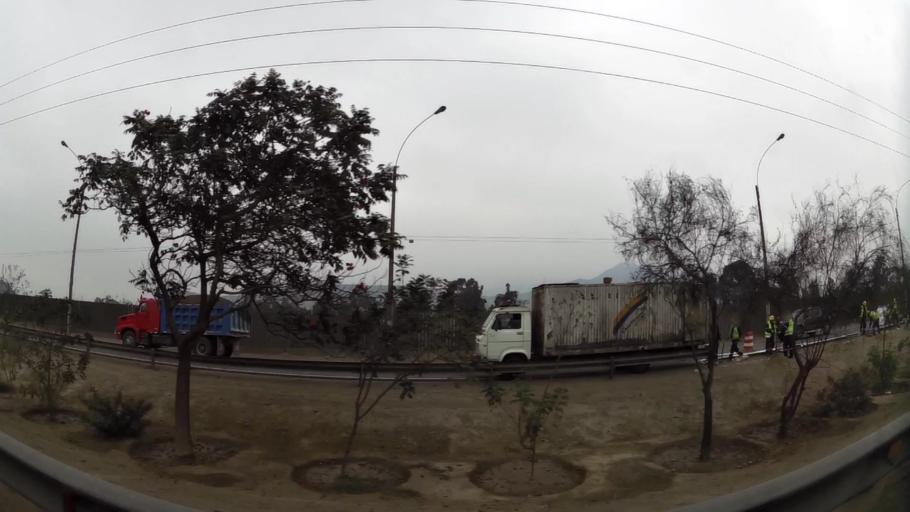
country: PE
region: Lima
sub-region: Lima
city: Vitarte
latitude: -12.0282
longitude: -76.9745
